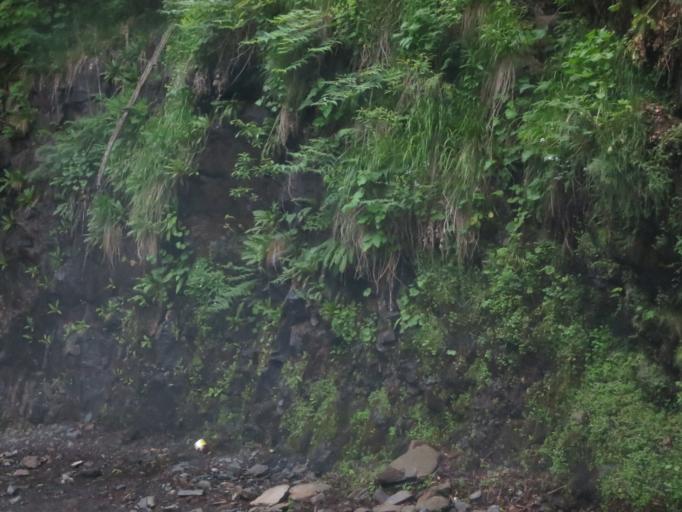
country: GE
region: Kakheti
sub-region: Telavi
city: Telavi
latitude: 42.2414
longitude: 45.4951
